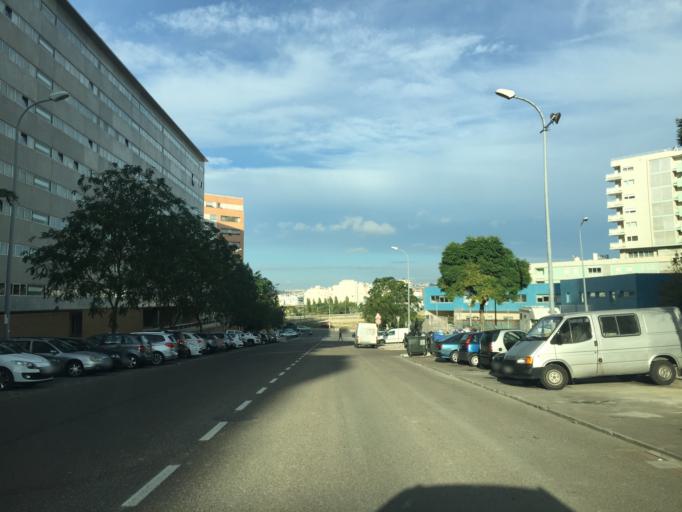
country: PT
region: Lisbon
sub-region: Odivelas
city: Olival do Basto
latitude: 38.7802
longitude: -9.1487
